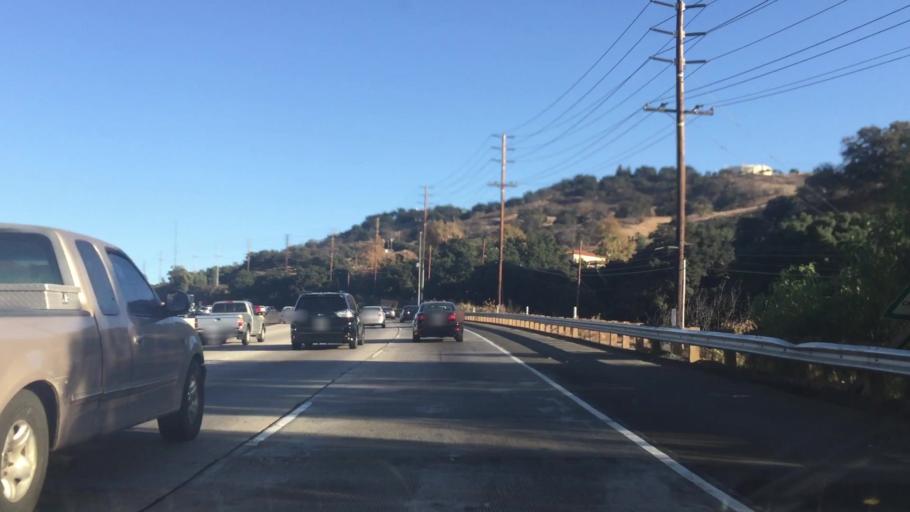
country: US
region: California
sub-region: Los Angeles County
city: Hidden Hills
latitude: 34.1496
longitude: -118.6751
